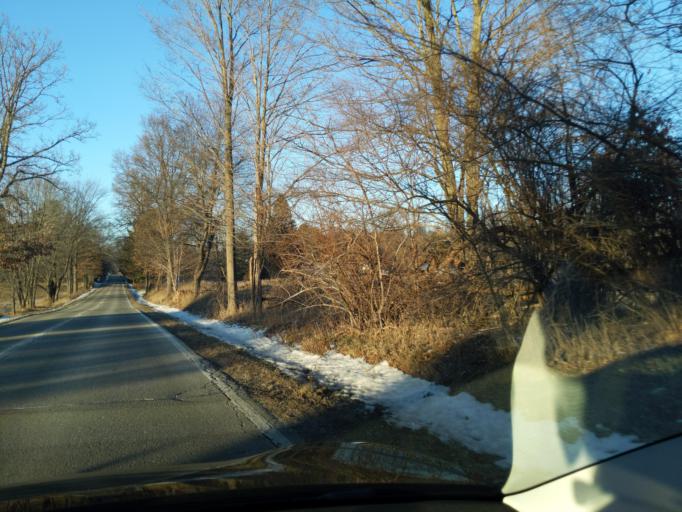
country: US
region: Michigan
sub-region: Ingham County
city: Stockbridge
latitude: 42.4505
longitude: -84.0762
